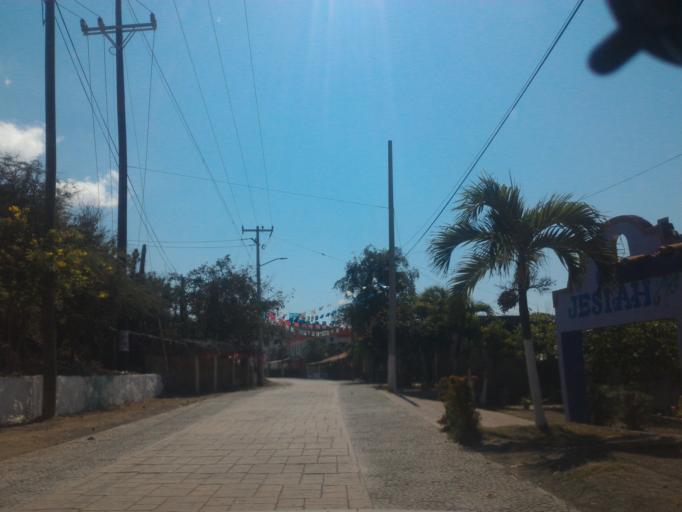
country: MX
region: Michoacan
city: Coahuayana Viejo
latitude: 18.5801
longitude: -103.6694
